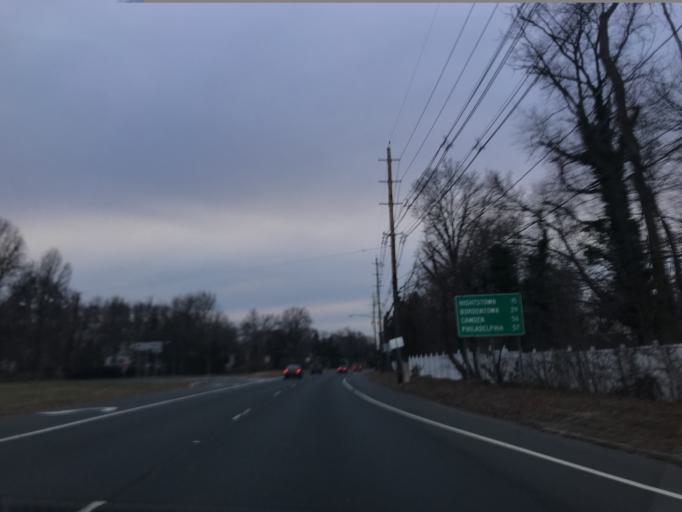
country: US
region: New Jersey
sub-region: Middlesex County
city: Milltown
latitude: 40.4533
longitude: -74.4586
